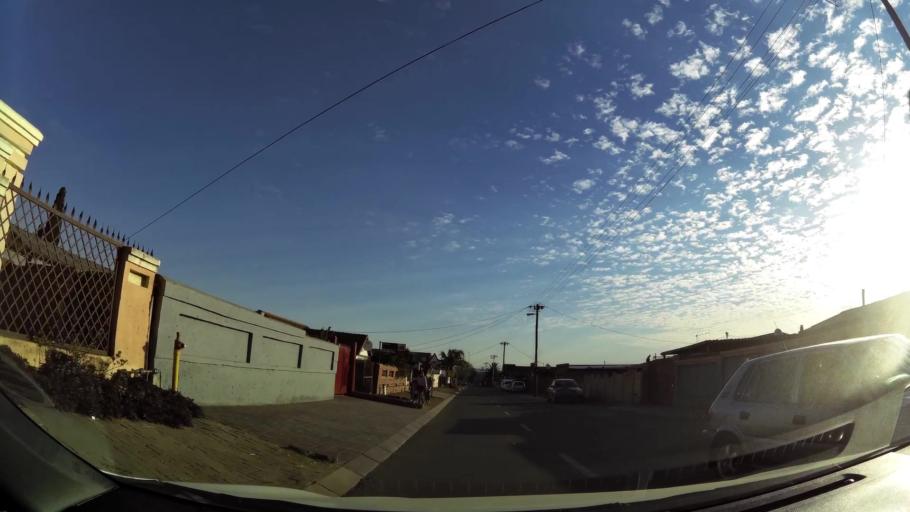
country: ZA
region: Gauteng
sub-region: City of Tshwane Metropolitan Municipality
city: Cullinan
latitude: -25.7120
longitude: 28.3732
